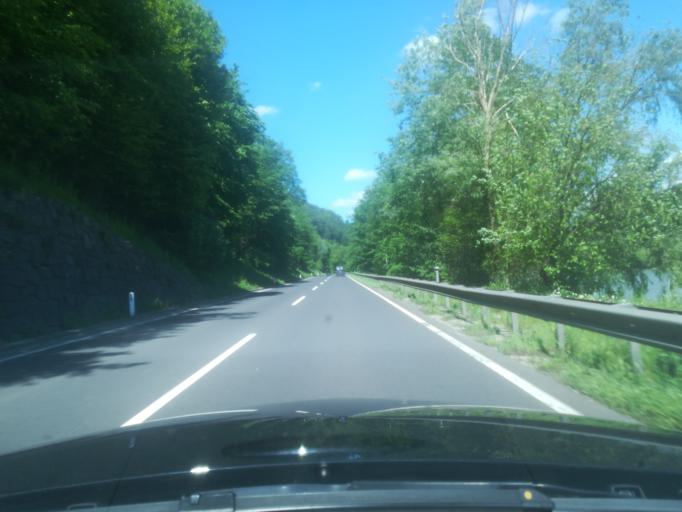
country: AT
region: Upper Austria
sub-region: Politischer Bezirk Urfahr-Umgebung
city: Ottensheim
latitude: 48.3120
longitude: 14.2140
